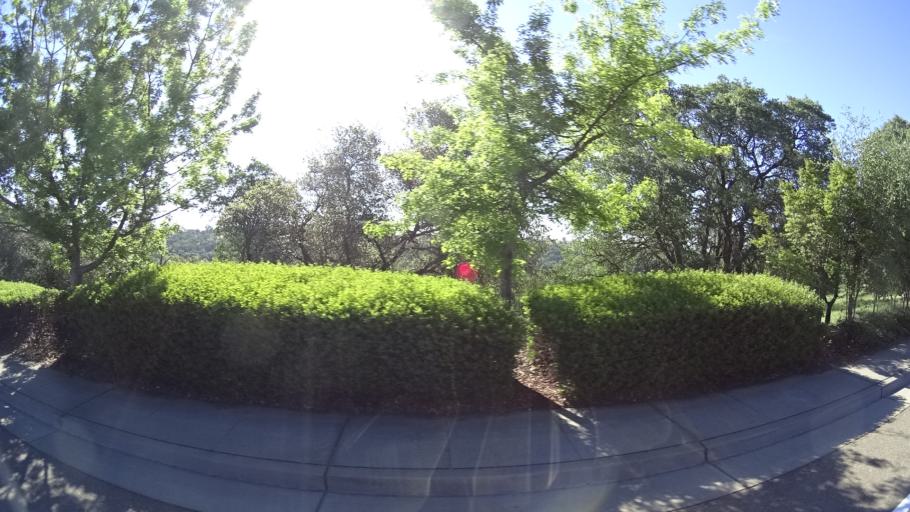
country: US
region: California
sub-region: Placer County
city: Rocklin
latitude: 38.8286
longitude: -121.2325
